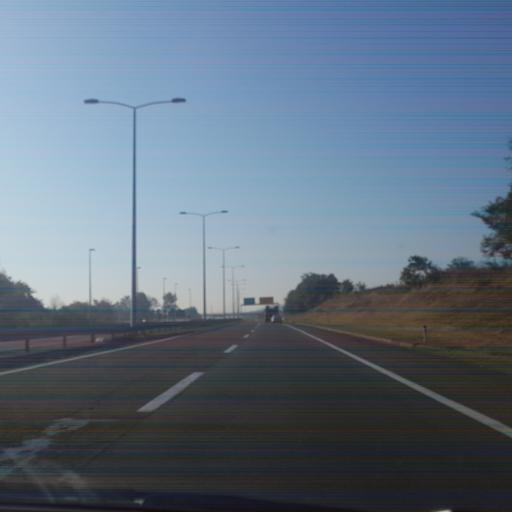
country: RS
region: Central Serbia
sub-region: Nisavski Okrug
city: Merosina
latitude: 43.2856
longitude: 21.8004
